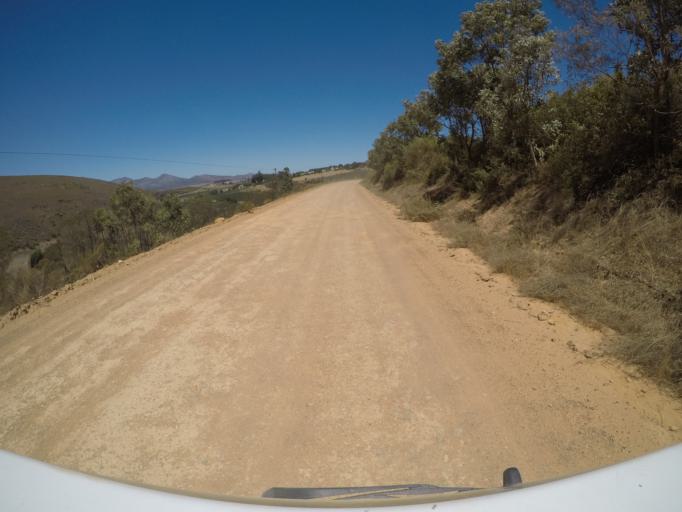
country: ZA
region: Western Cape
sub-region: Overberg District Municipality
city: Hermanus
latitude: -34.2159
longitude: 19.2093
